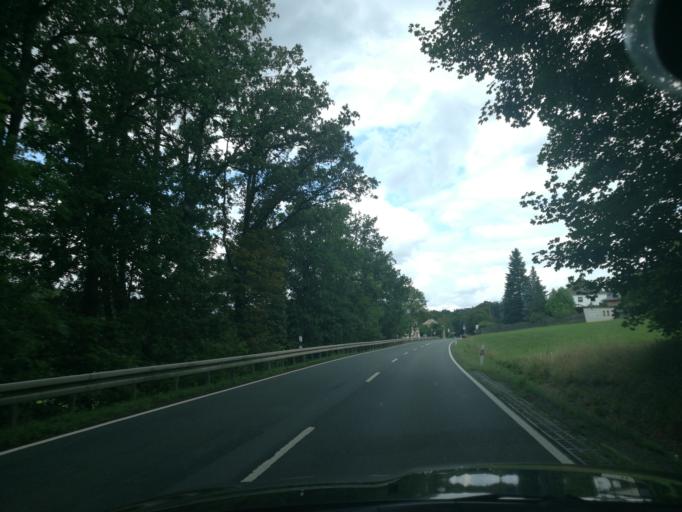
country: DE
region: Saxony
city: Oelsnitz
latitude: 50.3933
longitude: 12.1884
